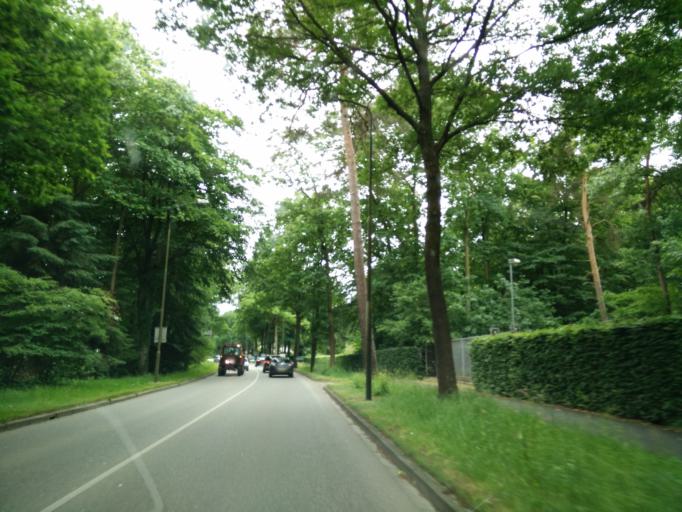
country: NL
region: Gelderland
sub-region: Gemeente Apeldoorn
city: Apeldoorn
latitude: 52.2091
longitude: 5.9305
